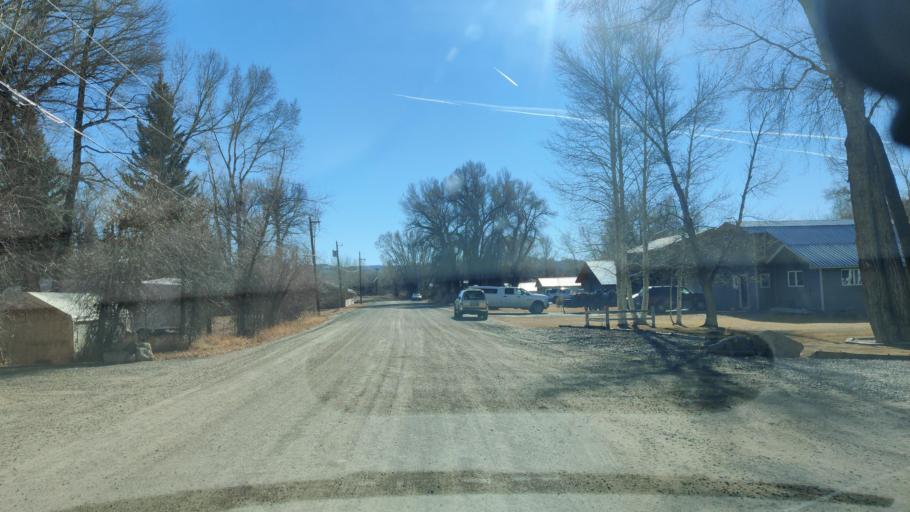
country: US
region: Colorado
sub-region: Gunnison County
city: Gunnison
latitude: 38.5352
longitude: -106.9512
